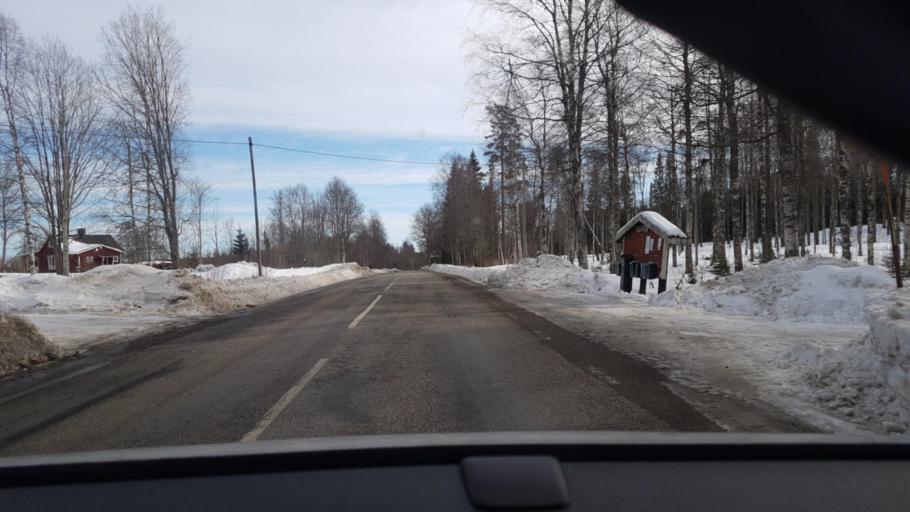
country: SE
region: Vaermland
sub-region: Arjangs Kommun
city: Arjaeng
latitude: 59.5776
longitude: 12.2307
